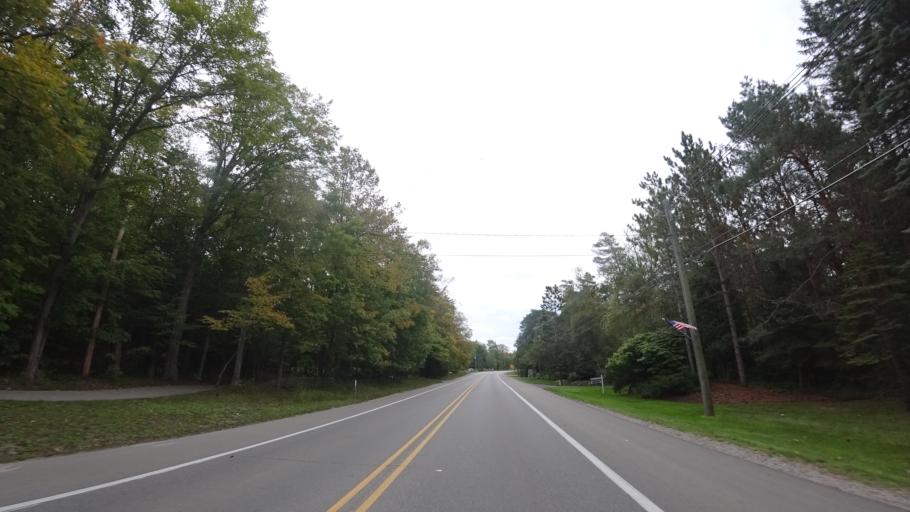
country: US
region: Michigan
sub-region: Emmet County
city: Harbor Springs
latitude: 45.4315
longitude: -84.9396
